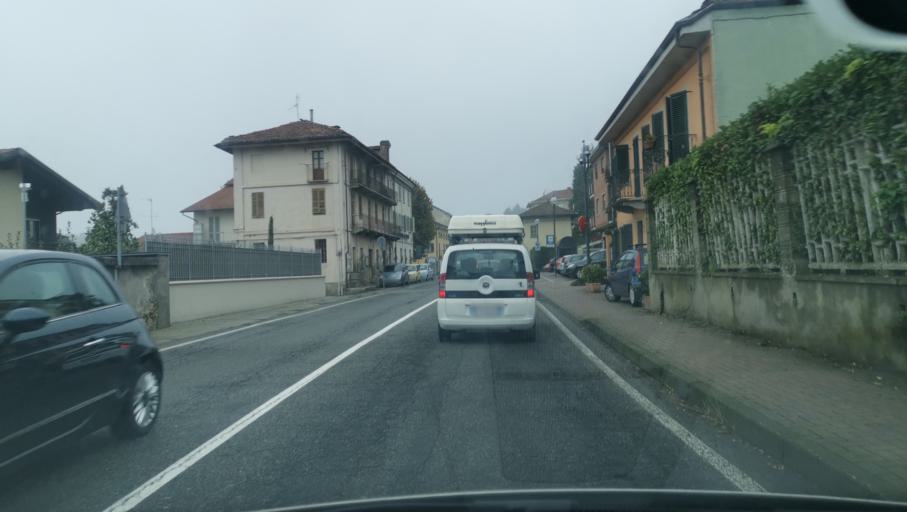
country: IT
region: Piedmont
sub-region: Provincia di Torino
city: Castiglione Torinese
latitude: 45.1216
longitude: 7.8138
